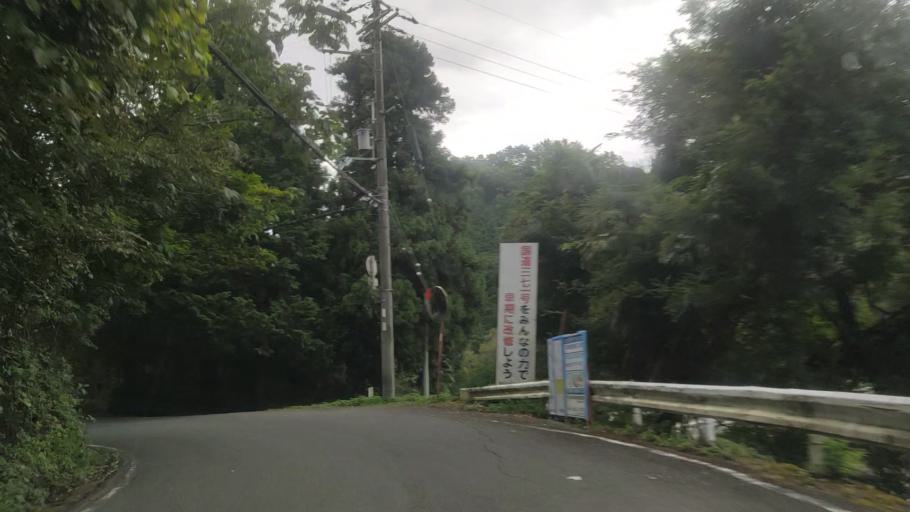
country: JP
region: Wakayama
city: Hashimoto
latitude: 34.3102
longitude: 135.6230
